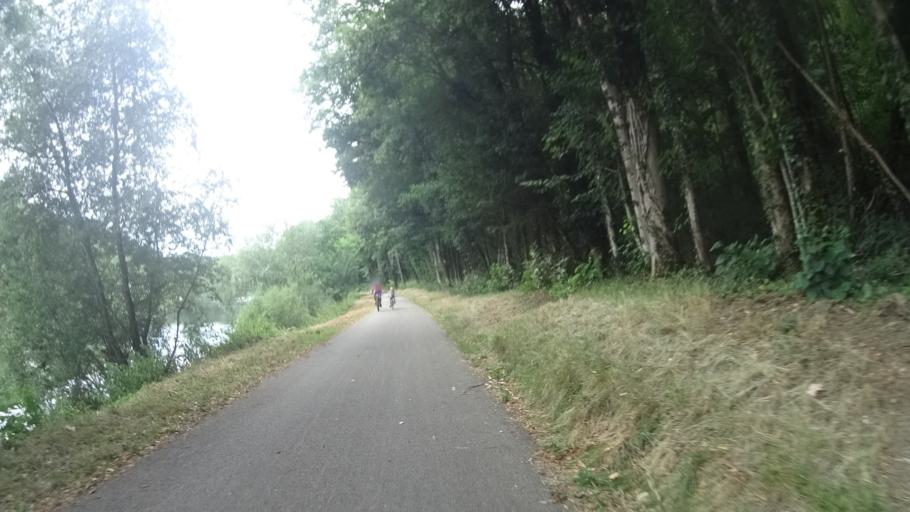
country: FR
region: Franche-Comte
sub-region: Departement du Doubs
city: Baume-les-Dames
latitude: 47.3407
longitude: 6.3408
